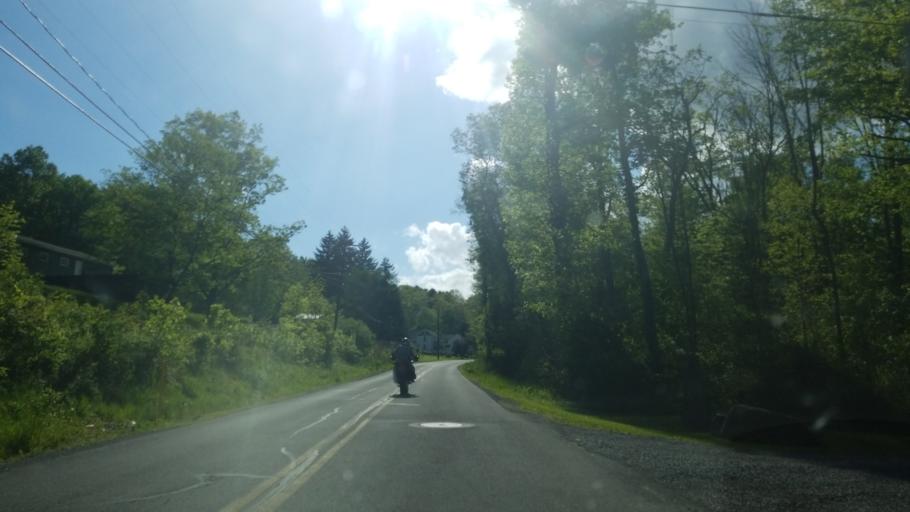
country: US
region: Pennsylvania
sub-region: Clearfield County
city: Troy
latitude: 40.9286
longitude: -78.2872
